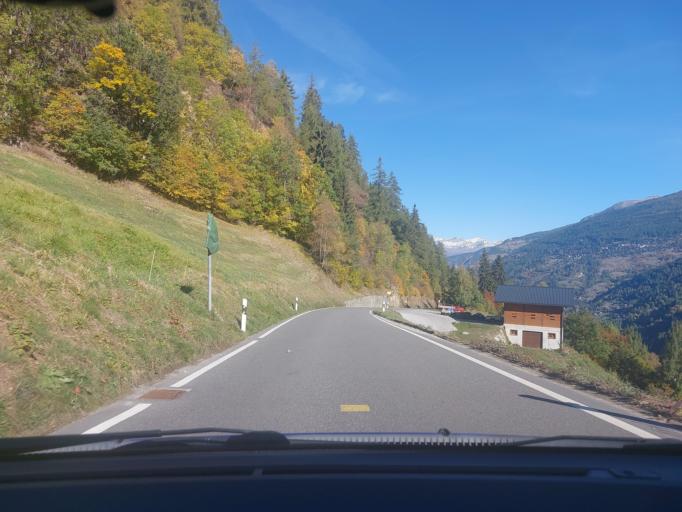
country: CH
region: Valais
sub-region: Sierre District
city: Chippis
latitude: 46.1852
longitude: 7.5847
